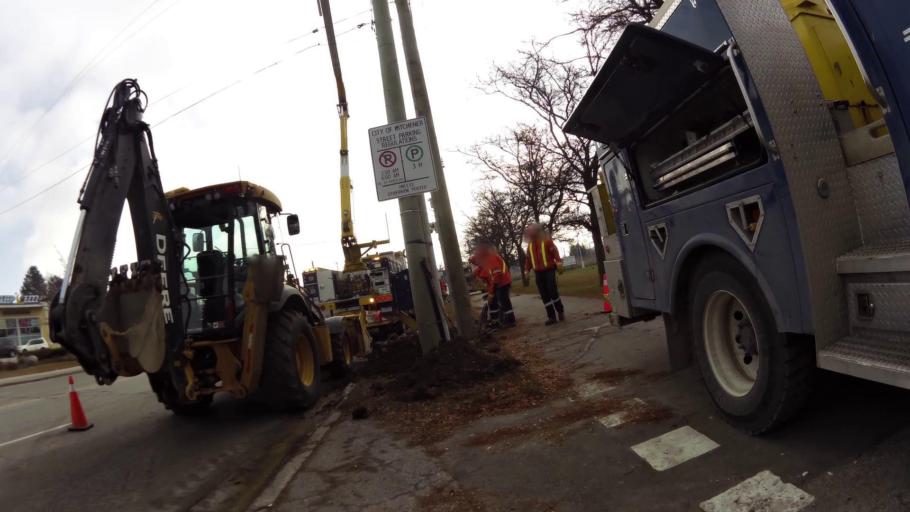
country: CA
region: Ontario
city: Kitchener
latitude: 43.4281
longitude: -80.4676
